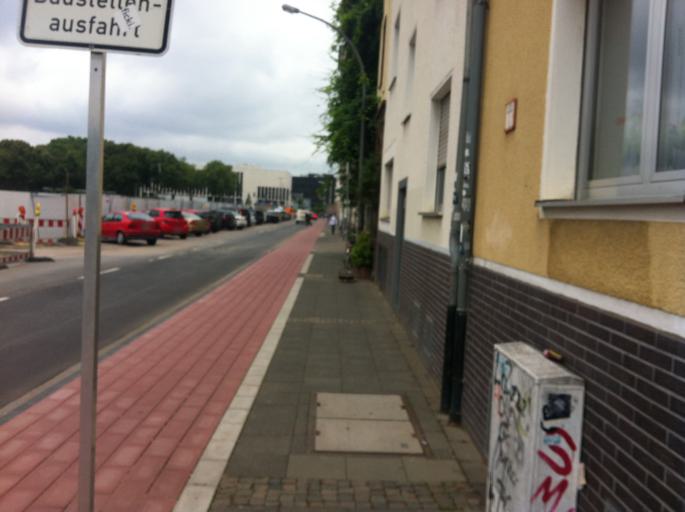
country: DE
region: North Rhine-Westphalia
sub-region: Regierungsbezirk Koln
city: Neustadt/Sued
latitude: 50.9238
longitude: 6.9393
